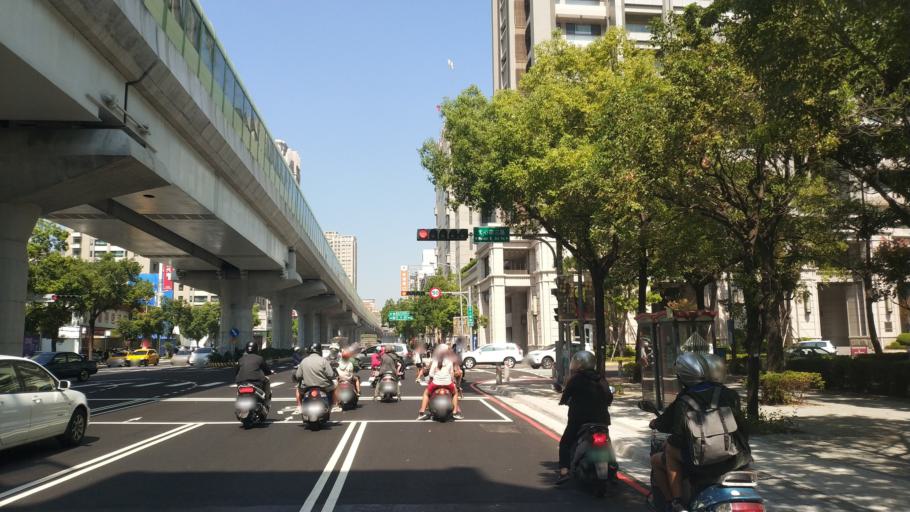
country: TW
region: Taiwan
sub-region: Taichung City
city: Taichung
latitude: 24.1328
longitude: 120.6466
